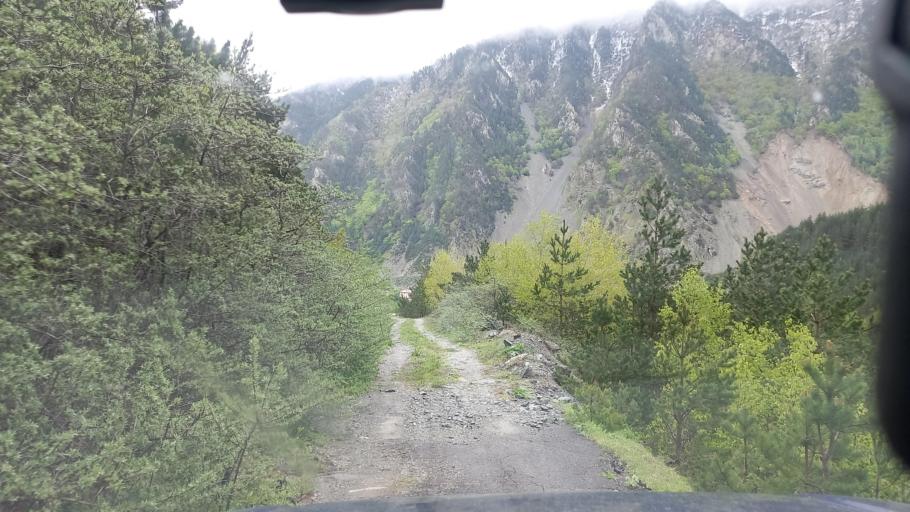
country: RU
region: North Ossetia
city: Mizur
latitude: 42.7916
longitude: 43.9967
